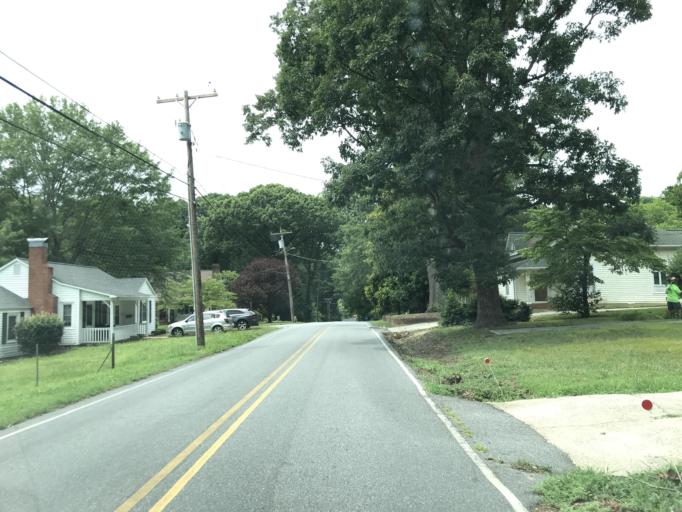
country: US
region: North Carolina
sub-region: Lincoln County
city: Lincolnton
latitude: 35.4797
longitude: -81.2508
